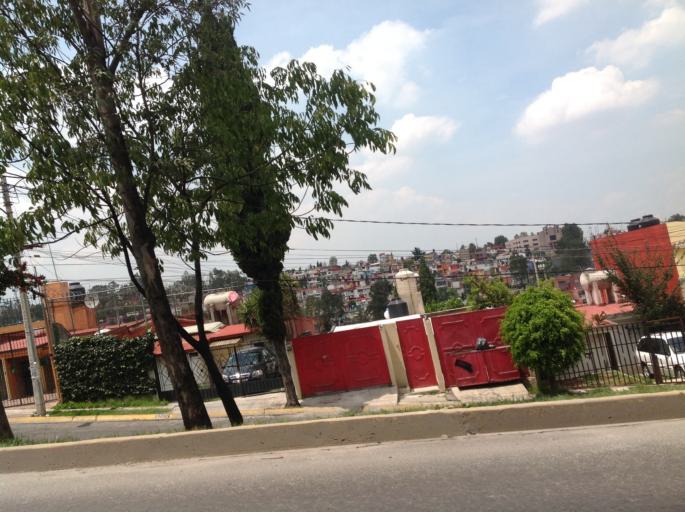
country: MX
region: Mexico
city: Ciudad Lopez Mateos
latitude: 19.5991
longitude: -99.2268
